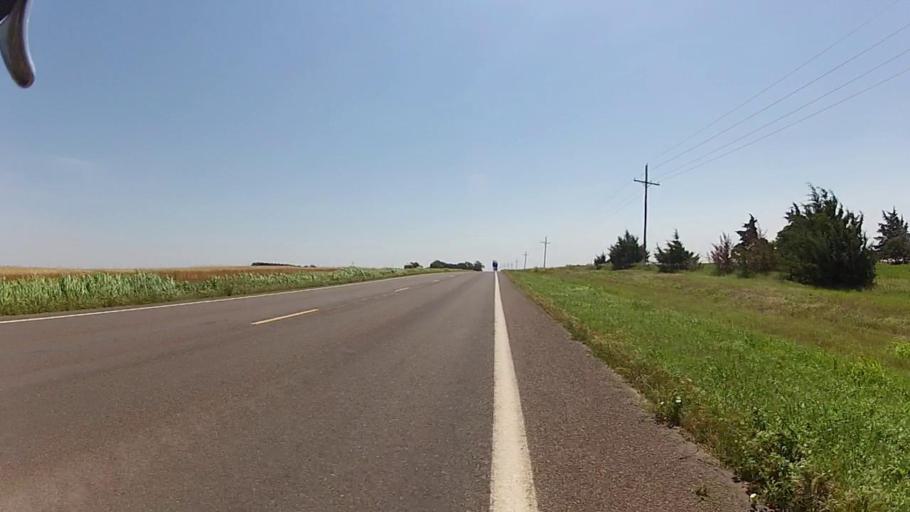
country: US
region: Kansas
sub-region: Sumner County
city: Caldwell
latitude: 37.0327
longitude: -97.5696
